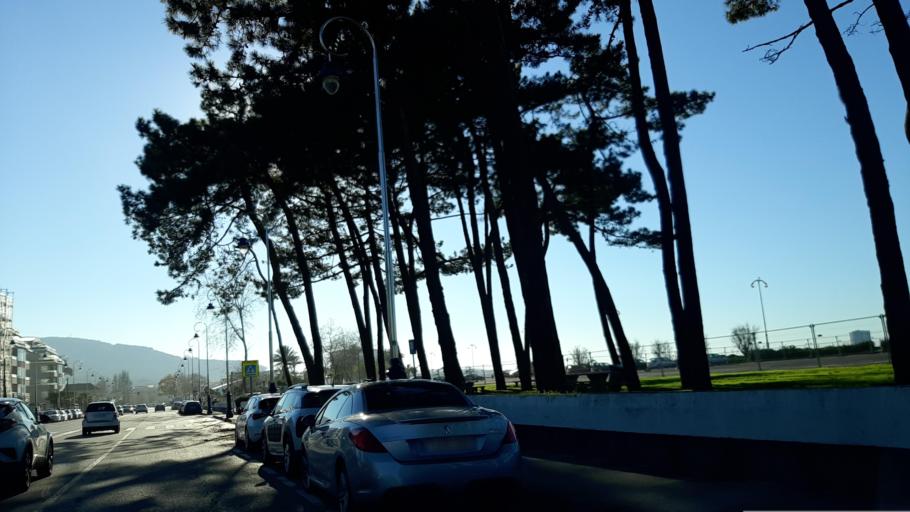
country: ES
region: Galicia
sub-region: Provincia de Pontevedra
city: Cangas
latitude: 42.2088
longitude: -8.7753
